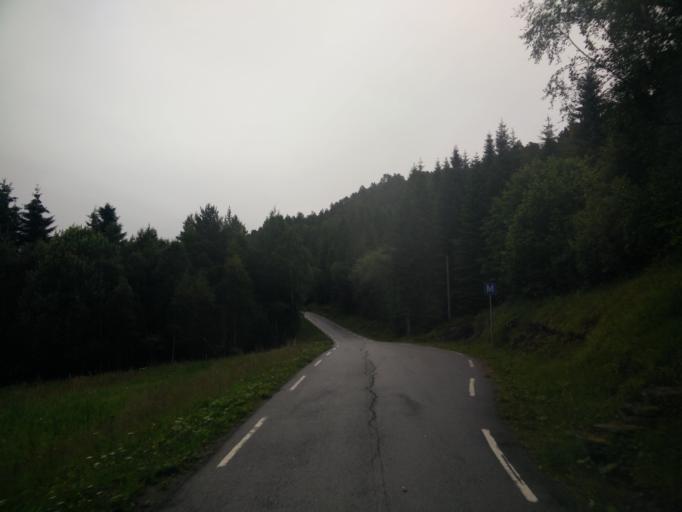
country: NO
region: More og Romsdal
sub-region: Kristiansund
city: Rensvik
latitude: 63.0302
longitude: 7.9095
